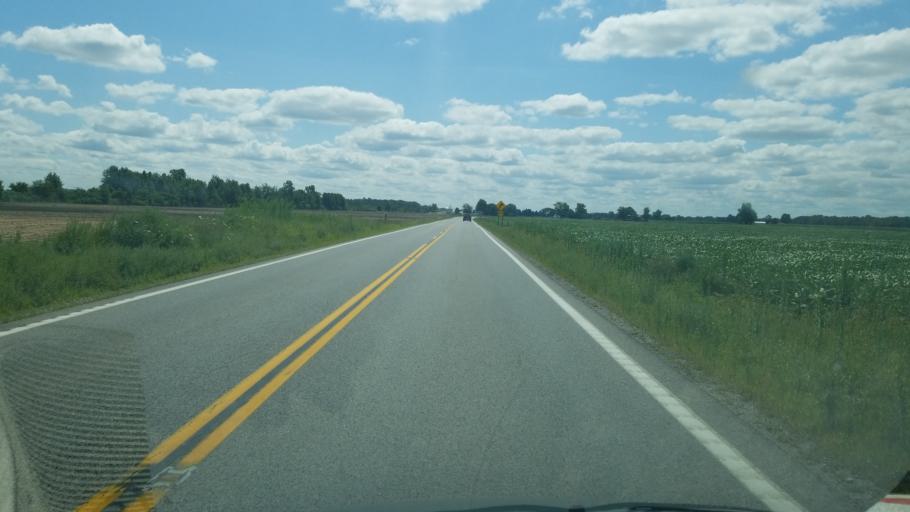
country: US
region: Ohio
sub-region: Fulton County
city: Delta
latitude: 41.6265
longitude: -84.0346
